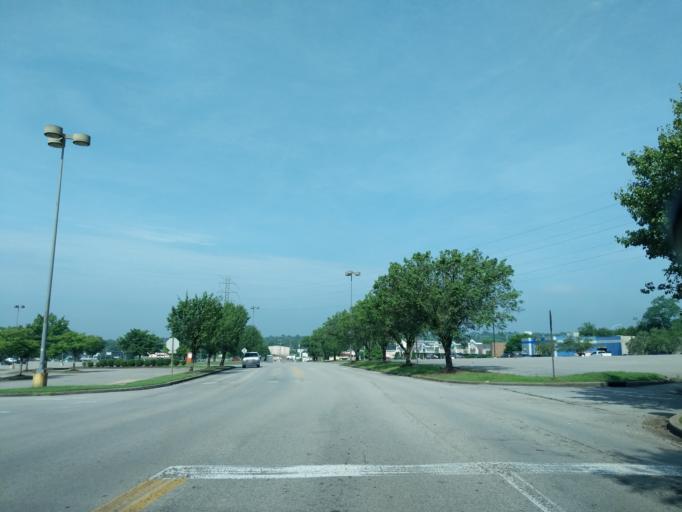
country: US
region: Tennessee
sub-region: Davidson County
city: Goodlettsville
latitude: 36.3050
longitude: -86.6980
